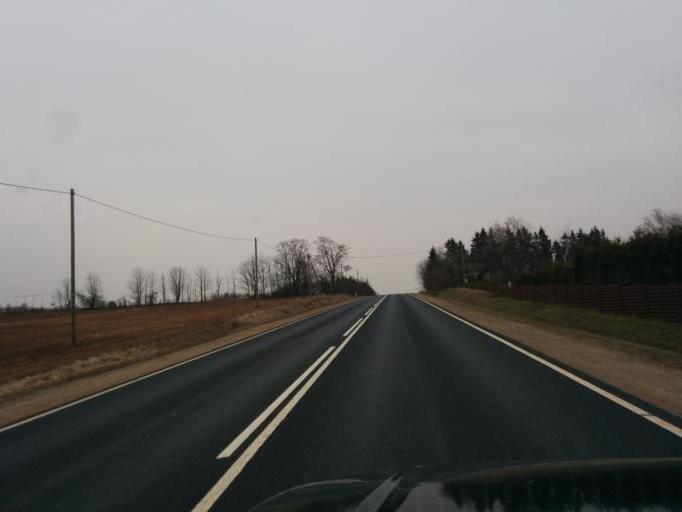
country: LV
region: Salaspils
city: Salaspils
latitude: 56.8268
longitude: 24.3367
